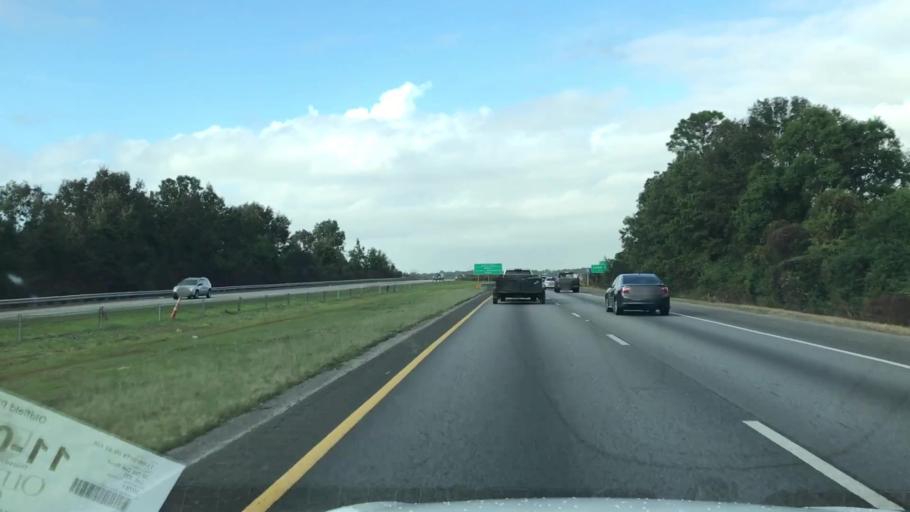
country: US
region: South Carolina
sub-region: Charleston County
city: North Charleston
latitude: 32.8270
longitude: -80.0298
